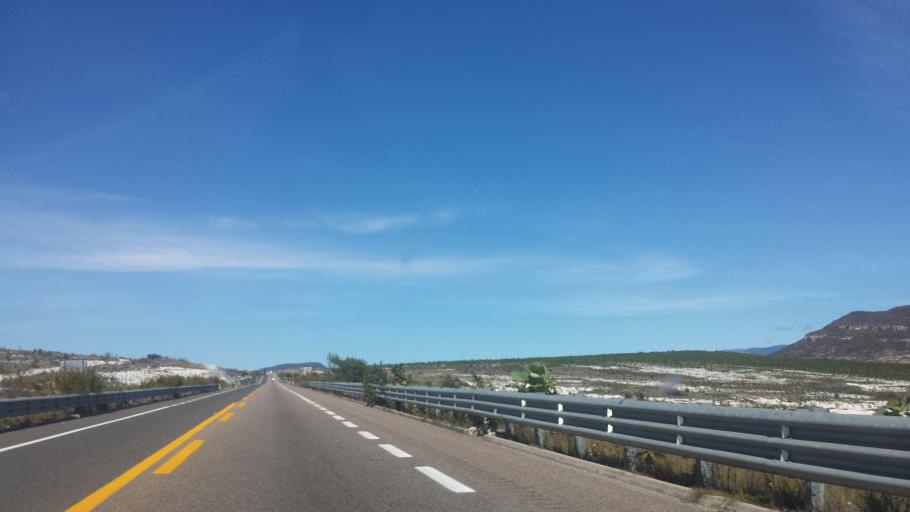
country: MX
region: Oaxaca
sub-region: Villa Tejupam de la Union
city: Villa Tejupam de la Union
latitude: 17.8334
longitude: -97.3730
